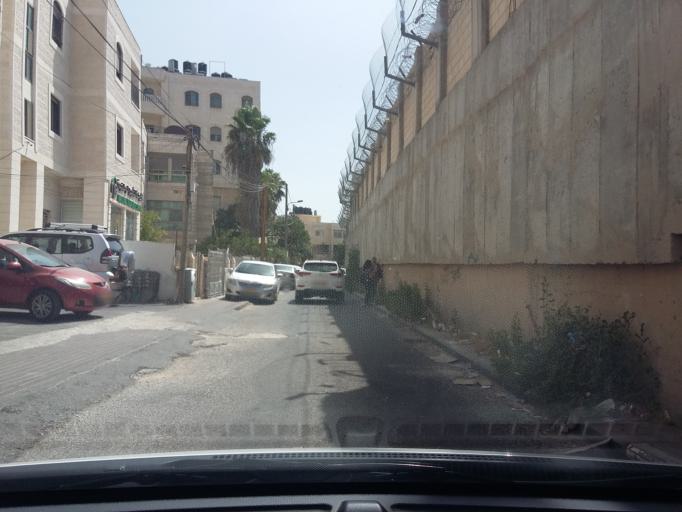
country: PS
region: West Bank
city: Ar Ram wa Dahiyat al Barid
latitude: 31.8445
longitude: 35.2330
